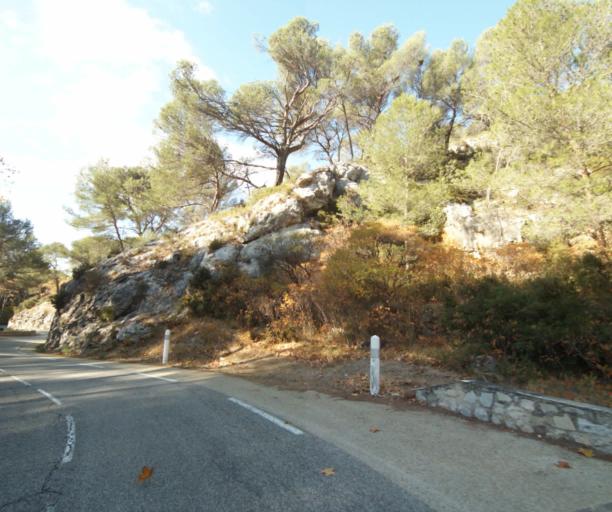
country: FR
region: Provence-Alpes-Cote d'Azur
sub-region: Departement des Bouches-du-Rhone
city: Saint-Savournin
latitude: 43.3712
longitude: 5.5084
